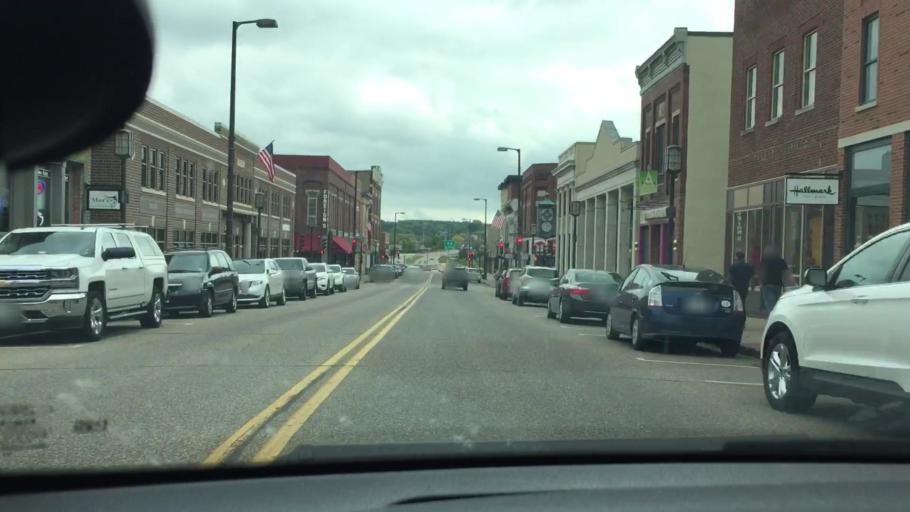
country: US
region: Wisconsin
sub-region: Chippewa County
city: Chippewa Falls
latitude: 44.9369
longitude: -91.3931
